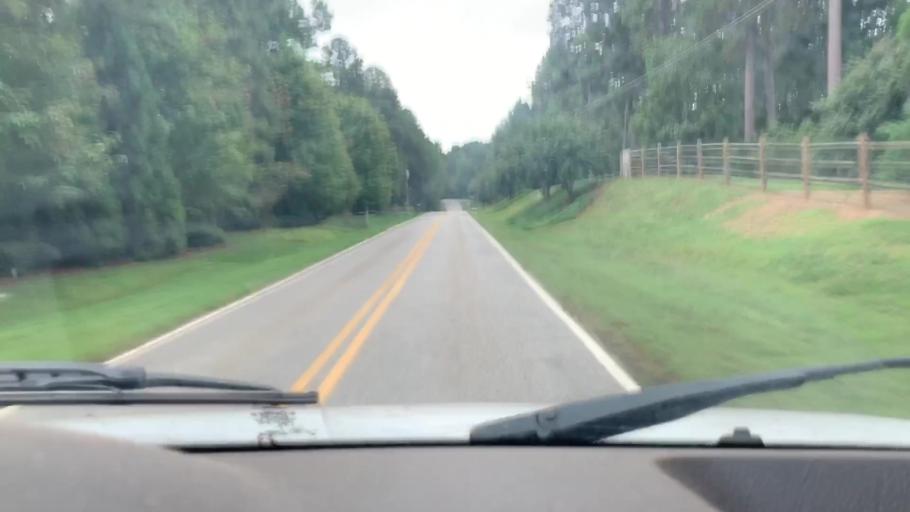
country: US
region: North Carolina
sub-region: Catawba County
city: Lake Norman of Catawba
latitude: 35.5509
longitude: -80.9062
